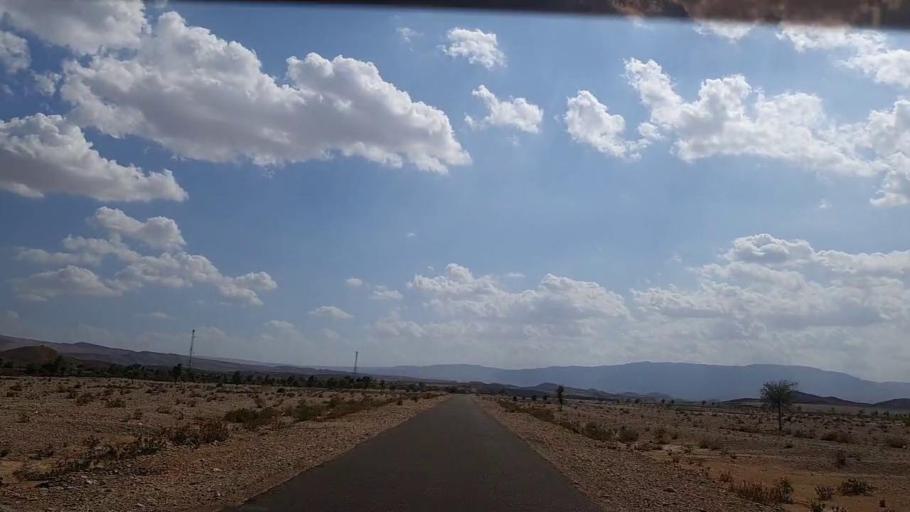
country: PK
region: Sindh
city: Johi
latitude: 26.5024
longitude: 67.4384
